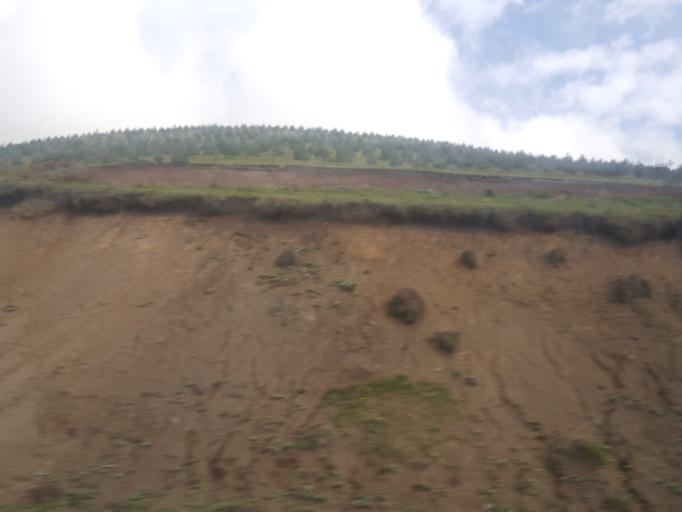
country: TR
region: Tokat
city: Bereketli
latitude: 40.5886
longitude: 37.2978
